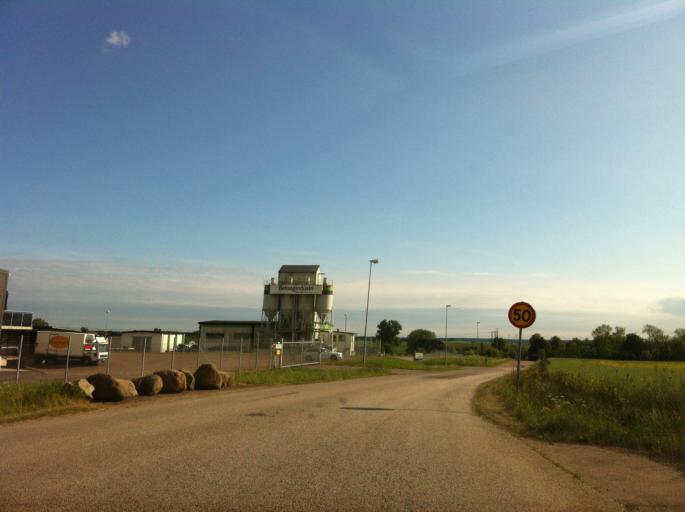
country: SE
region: Skane
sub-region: Svalovs Kommun
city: Kagerod
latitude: 55.9876
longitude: 13.0749
